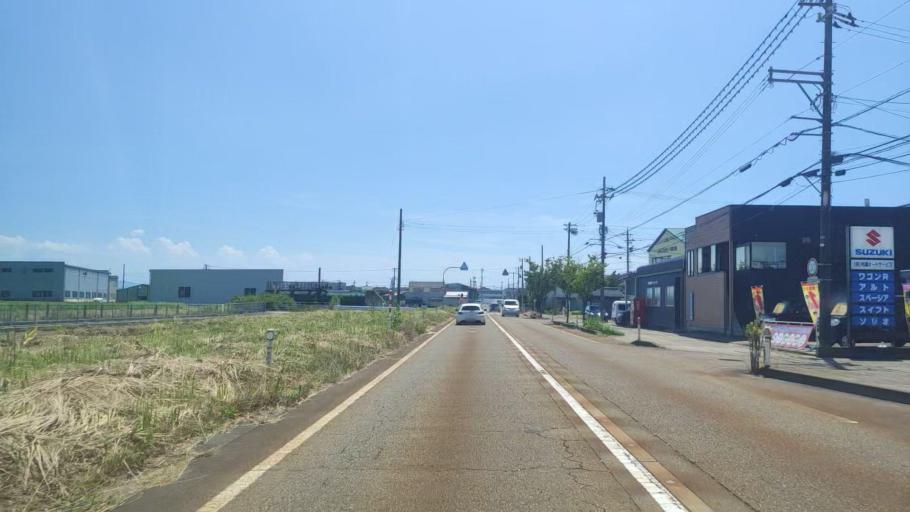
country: JP
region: Ishikawa
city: Kanazawa-shi
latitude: 36.6500
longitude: 136.6504
